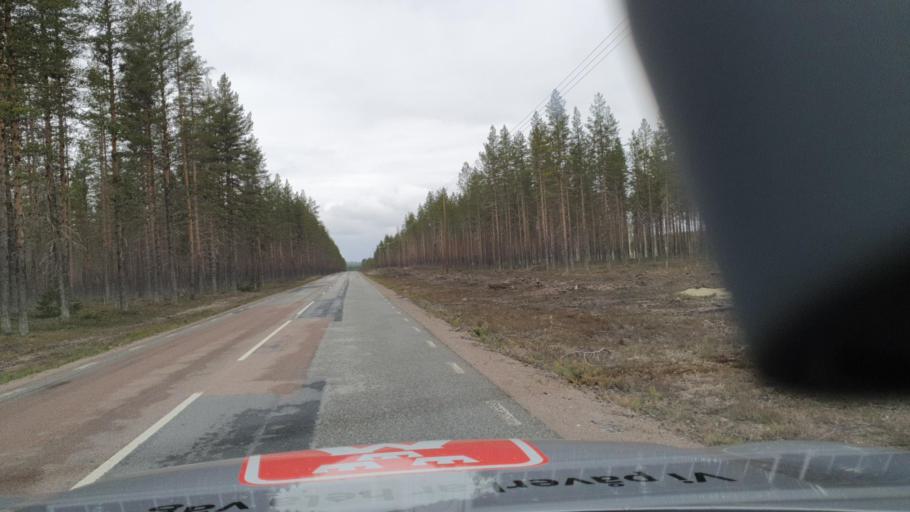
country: SE
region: Vaesternorrland
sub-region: Solleftea Kommun
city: Solleftea
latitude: 63.6139
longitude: 17.5007
